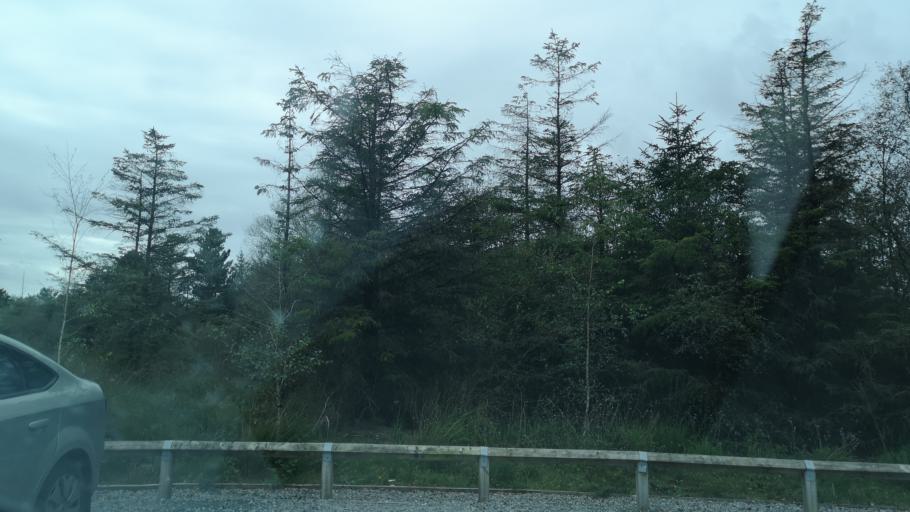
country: IE
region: Leinster
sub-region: Uibh Fhaili
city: Ferbane
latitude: 53.2234
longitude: -7.7291
